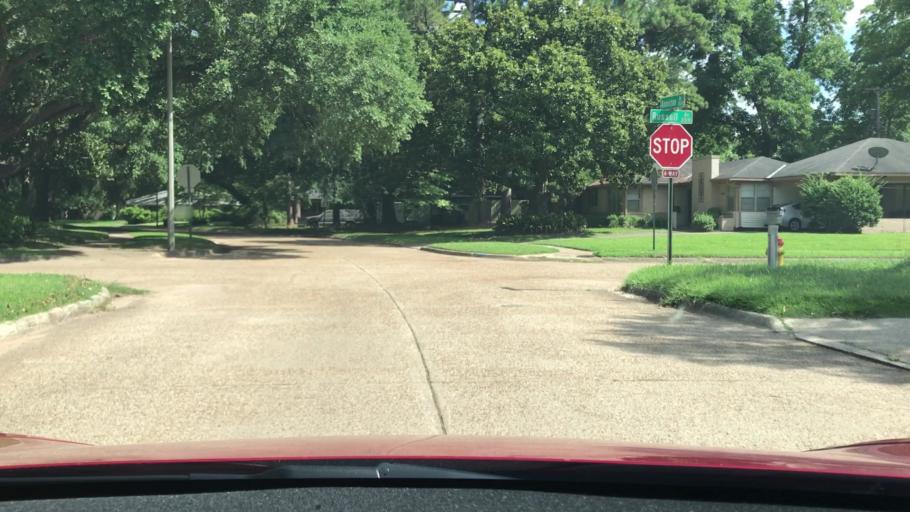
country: US
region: Louisiana
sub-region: Bossier Parish
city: Bossier City
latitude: 32.4613
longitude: -93.7133
